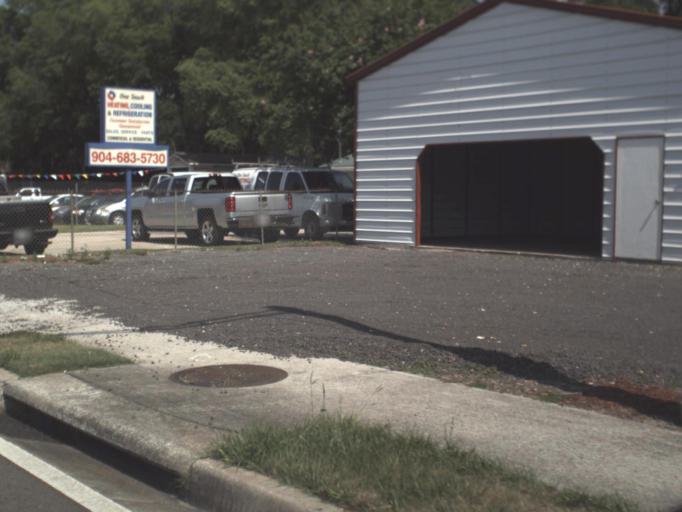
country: US
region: Florida
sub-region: Clay County
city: Bellair-Meadowbrook Terrace
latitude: 30.2481
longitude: -81.7866
